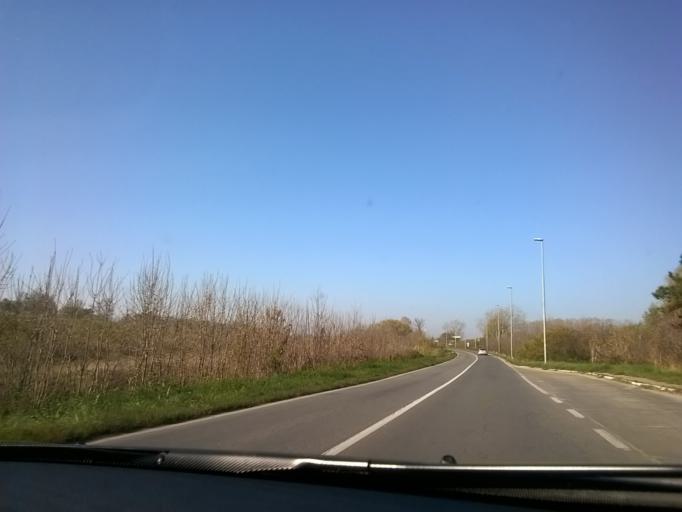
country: RS
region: Autonomna Pokrajina Vojvodina
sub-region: Juznobanatski Okrug
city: Pancevo
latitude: 44.8696
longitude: 20.6193
